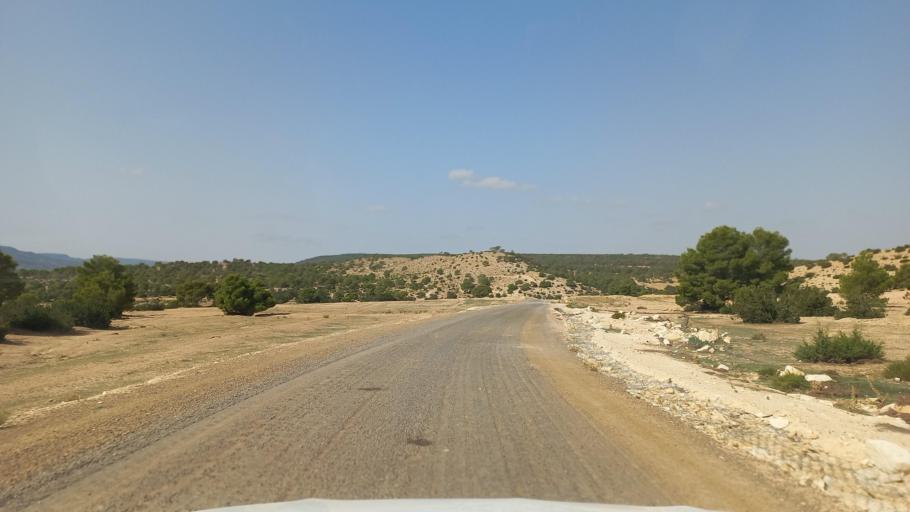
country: TN
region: Al Qasrayn
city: Sbiba
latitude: 35.3972
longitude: 8.9530
